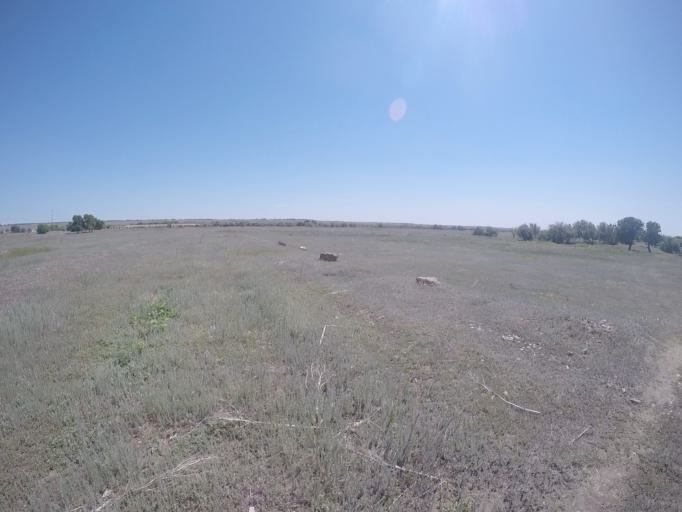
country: RU
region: Saratov
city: Krasnoarmeysk
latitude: 51.1679
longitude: 45.9033
